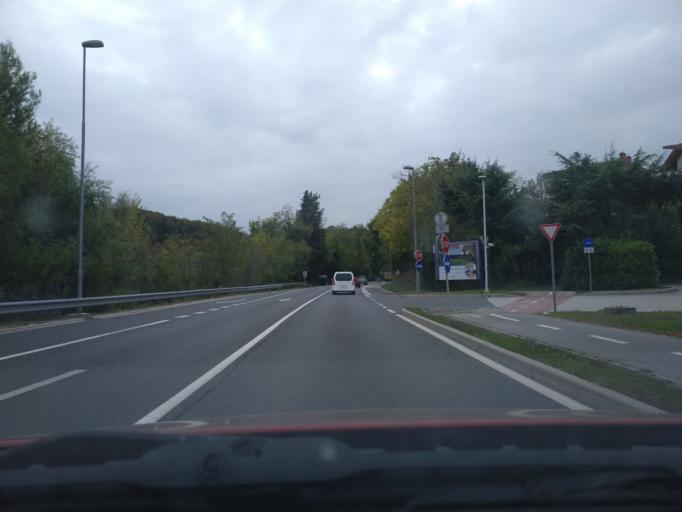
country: SI
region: Nova Gorica
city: Nova Gorica
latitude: 45.9533
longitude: 13.6527
